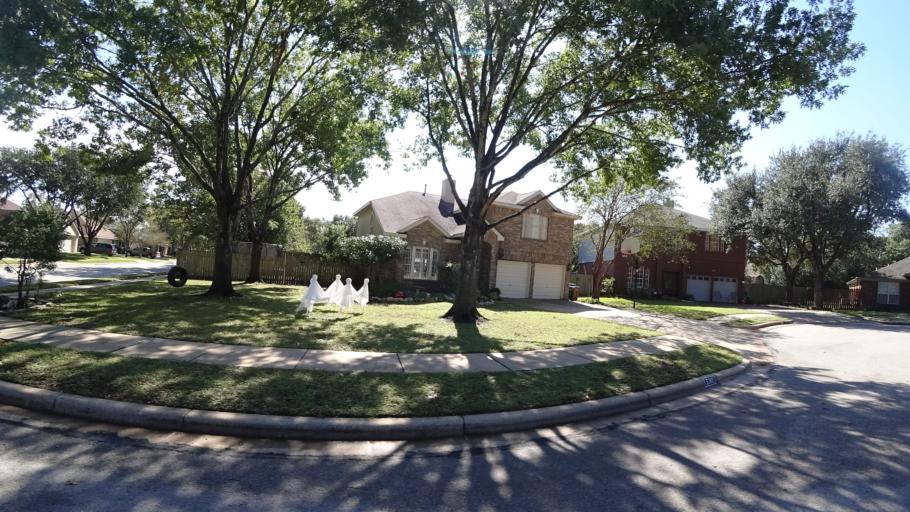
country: US
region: Texas
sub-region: Travis County
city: Shady Hollow
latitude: 30.2188
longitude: -97.8571
